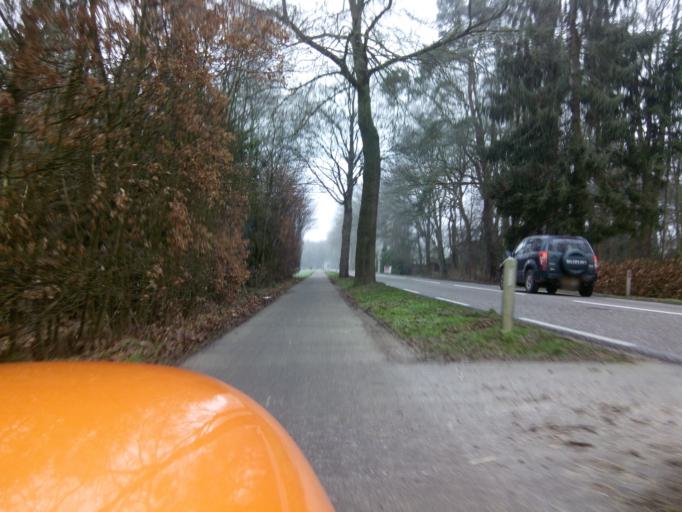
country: NL
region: Gelderland
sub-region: Gemeente Barneveld
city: Voorthuizen
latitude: 52.2001
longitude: 5.6079
